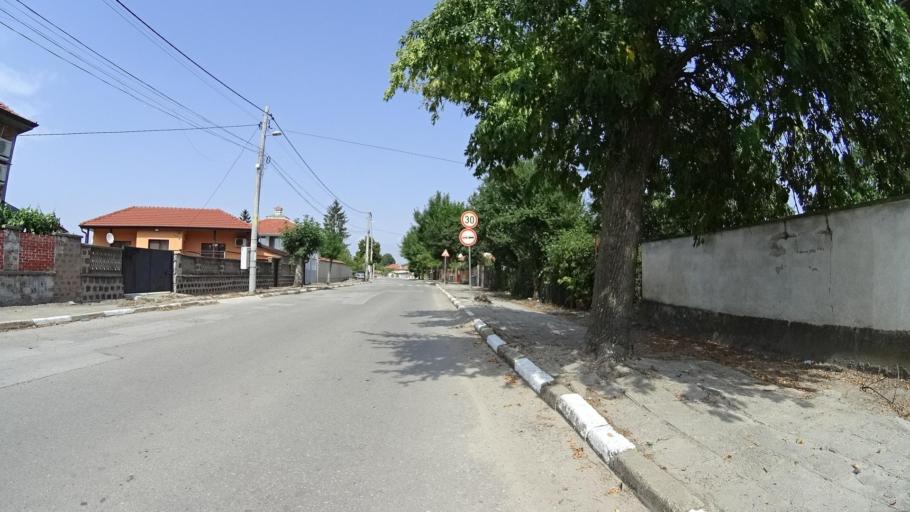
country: BG
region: Plovdiv
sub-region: Obshtina Plovdiv
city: Plovdiv
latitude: 42.2397
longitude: 24.7920
